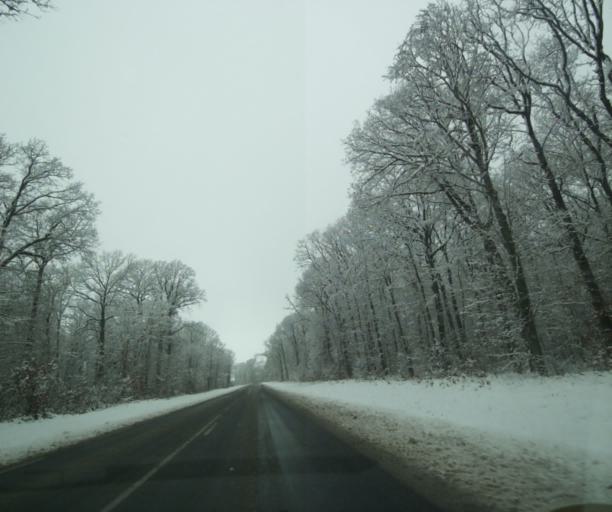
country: FR
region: Champagne-Ardenne
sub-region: Departement de la Haute-Marne
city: Montier-en-Der
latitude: 48.5425
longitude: 4.8286
